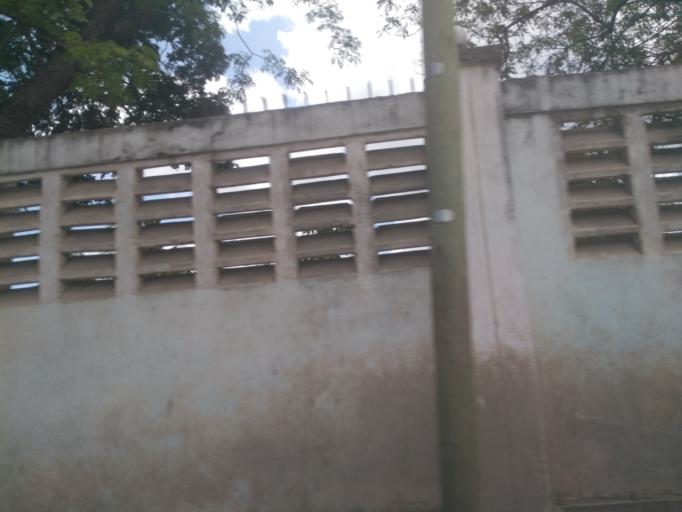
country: TZ
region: Dar es Salaam
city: Dar es Salaam
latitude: -6.8361
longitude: 39.2840
